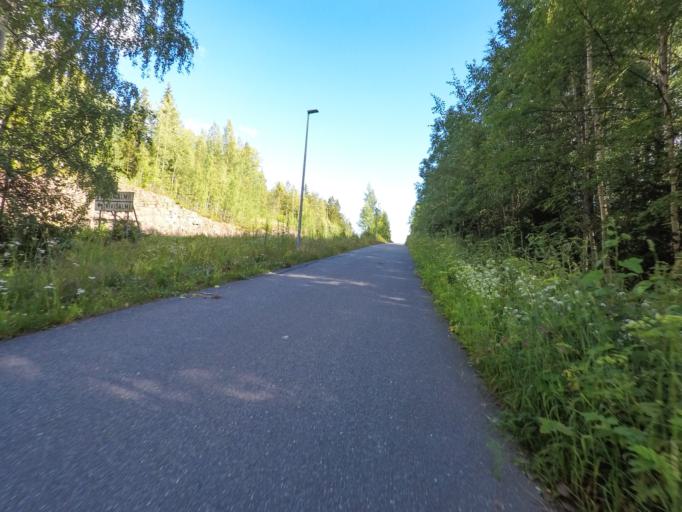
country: FI
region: South Karelia
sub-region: Lappeenranta
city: Lappeenranta
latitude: 61.0926
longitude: 28.1397
